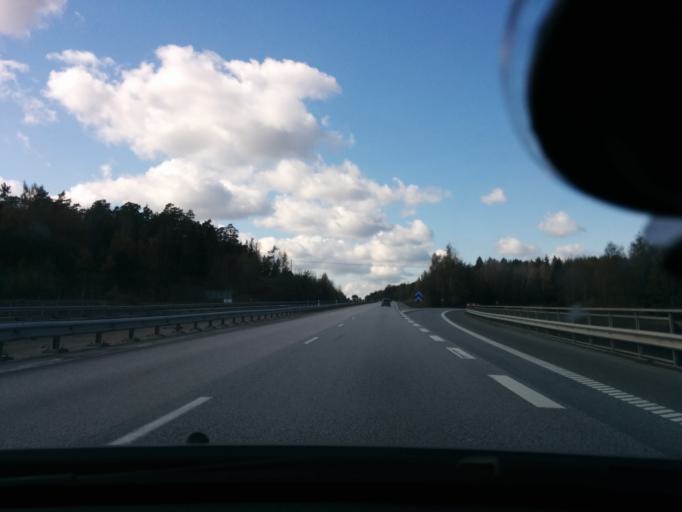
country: SE
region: Stockholm
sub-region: Upplands-Bro Kommun
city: Bro
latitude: 59.5309
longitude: 17.6317
